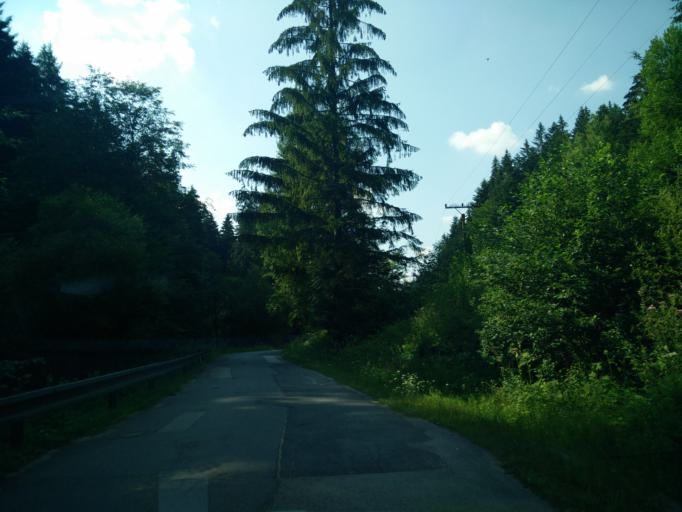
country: SK
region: Zilinsky
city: Rajec
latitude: 49.0894
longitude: 18.7311
